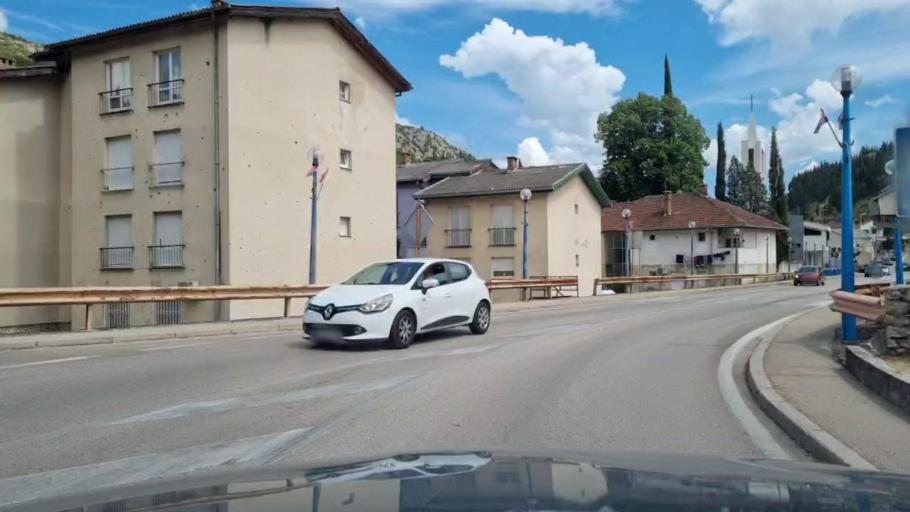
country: BA
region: Federation of Bosnia and Herzegovina
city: Stolac
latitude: 43.0842
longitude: 17.9570
